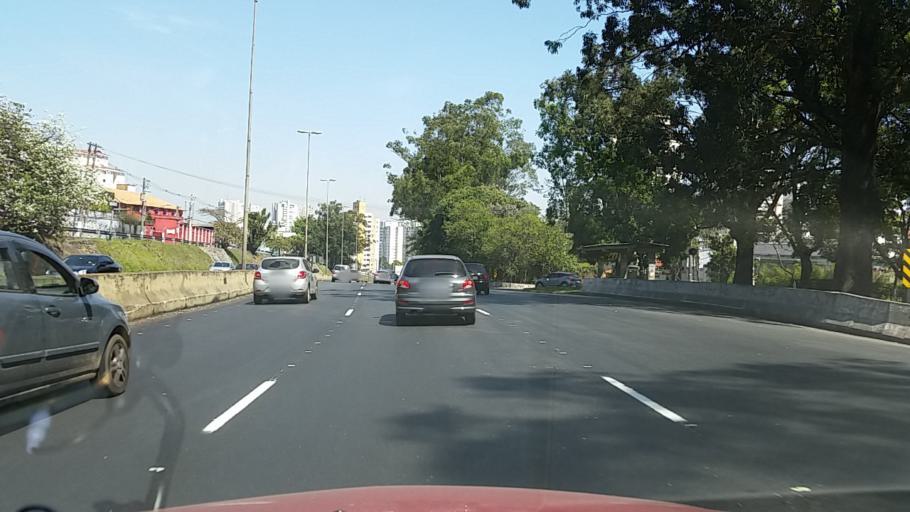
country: BR
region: Sao Paulo
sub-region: Taboao Da Serra
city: Taboao da Serra
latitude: -23.5825
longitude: -46.7332
